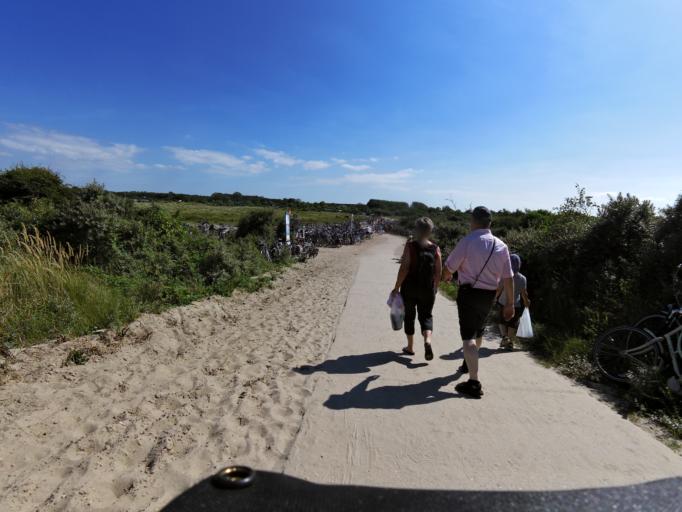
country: NL
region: Zeeland
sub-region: Schouwen-Duiveland
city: Renesse
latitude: 51.7372
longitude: 3.7520
